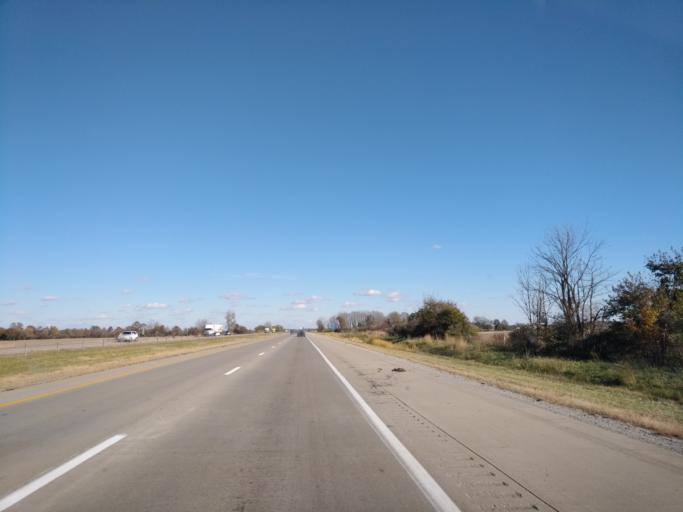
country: US
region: Indiana
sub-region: Marion County
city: Cumberland
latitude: 39.8196
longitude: -85.8741
